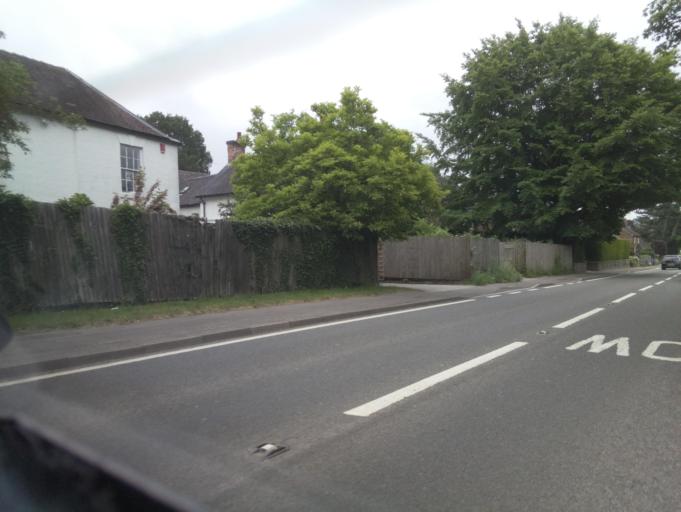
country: GB
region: England
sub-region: Derbyshire
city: Yeldersley
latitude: 52.9683
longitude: -1.6193
